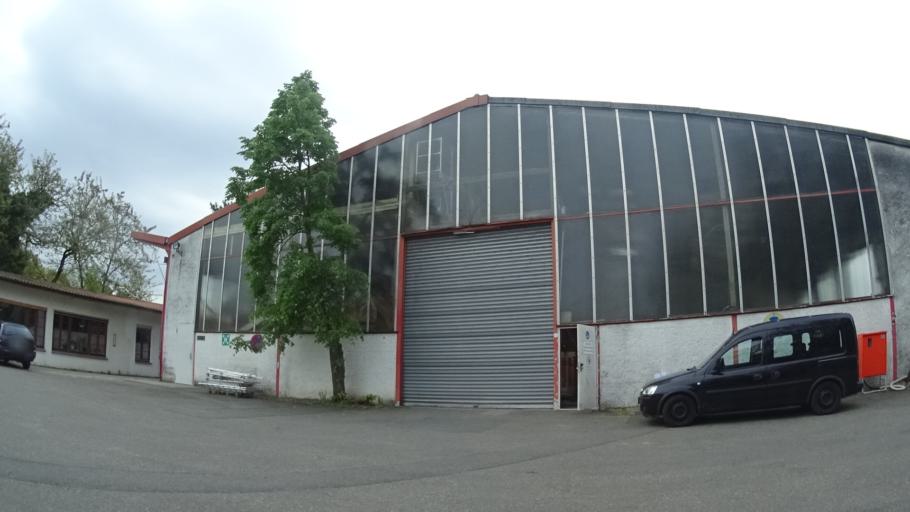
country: DE
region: Baden-Wuerttemberg
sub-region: Karlsruhe Region
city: Bruhl
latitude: 49.4037
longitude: 8.5591
